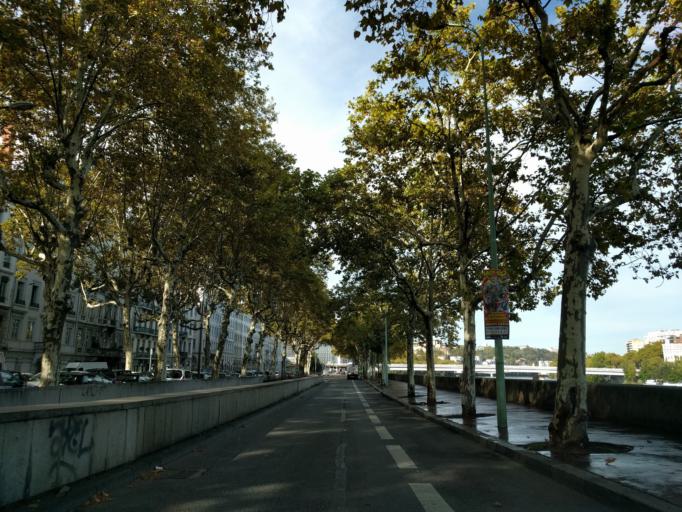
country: FR
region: Rhone-Alpes
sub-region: Departement du Rhone
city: Caluire-et-Cuire
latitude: 45.7693
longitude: 4.8382
